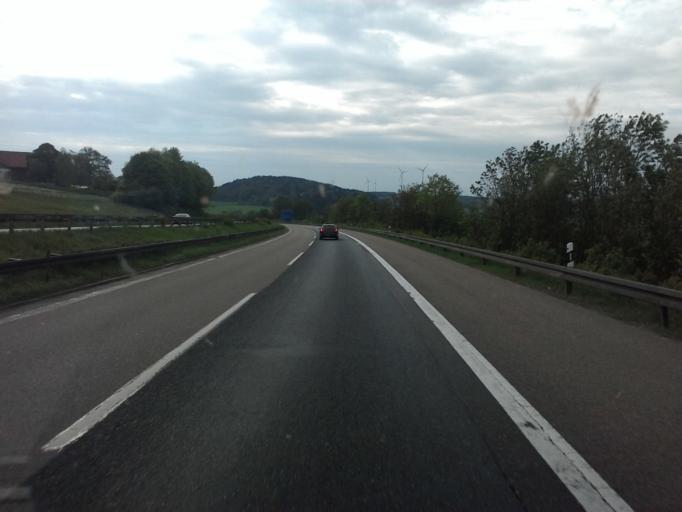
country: DE
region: Bavaria
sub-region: Upper Palatinate
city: Deining
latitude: 49.2796
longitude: 11.5931
